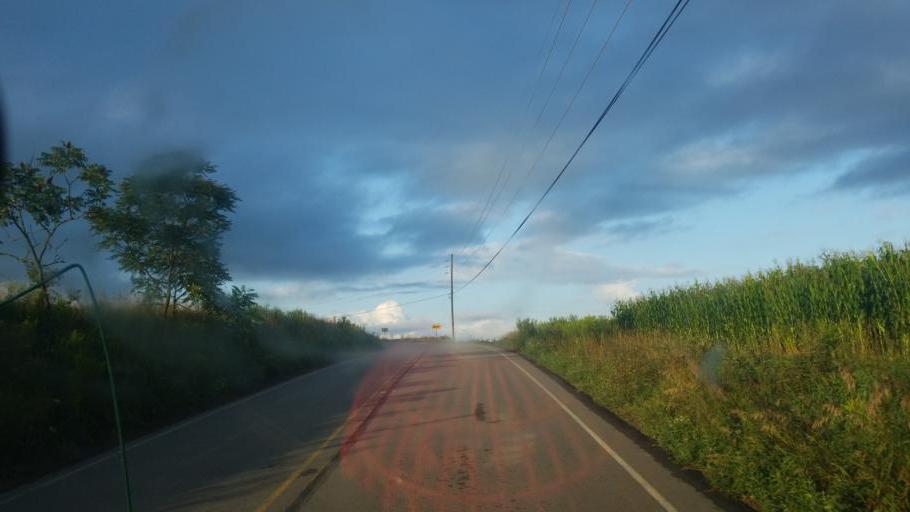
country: US
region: Pennsylvania
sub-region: Potter County
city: Galeton
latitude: 41.8914
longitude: -77.7609
